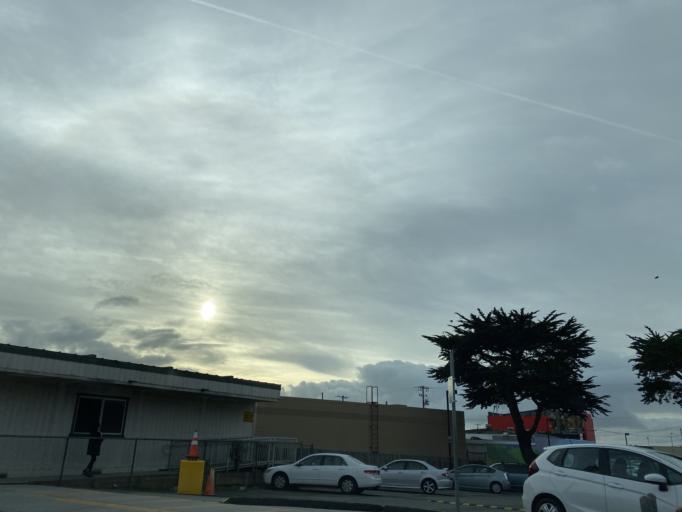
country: US
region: California
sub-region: San Mateo County
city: Pacifica
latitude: 37.6498
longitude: -122.4893
